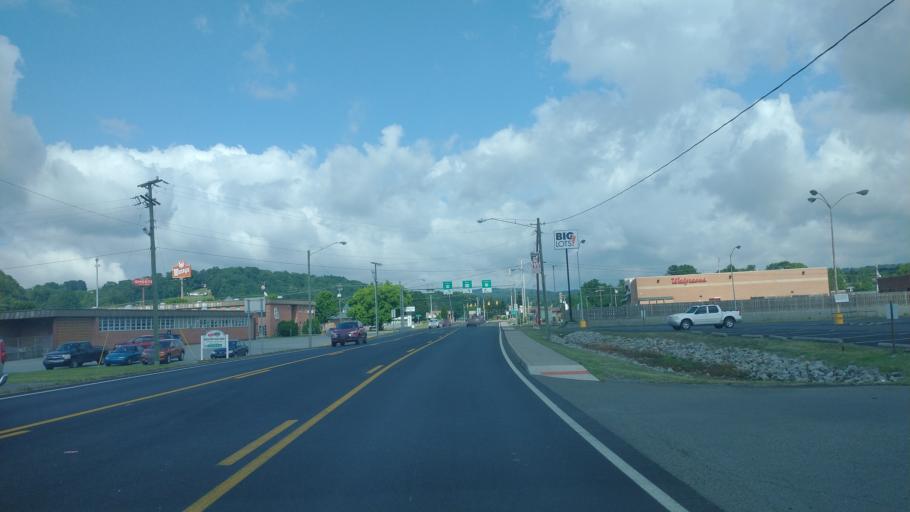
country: US
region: West Virginia
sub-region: Mercer County
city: Princeton
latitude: 37.3604
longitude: -81.1029
